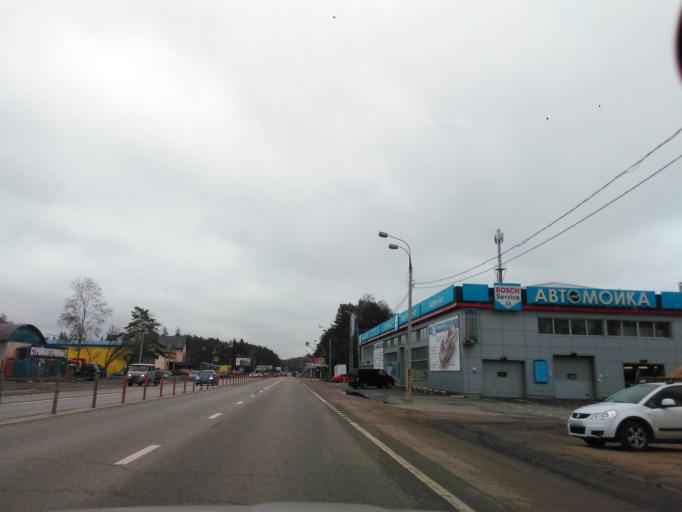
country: RU
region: Moskovskaya
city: Nakhabino
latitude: 55.8445
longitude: 37.2014
